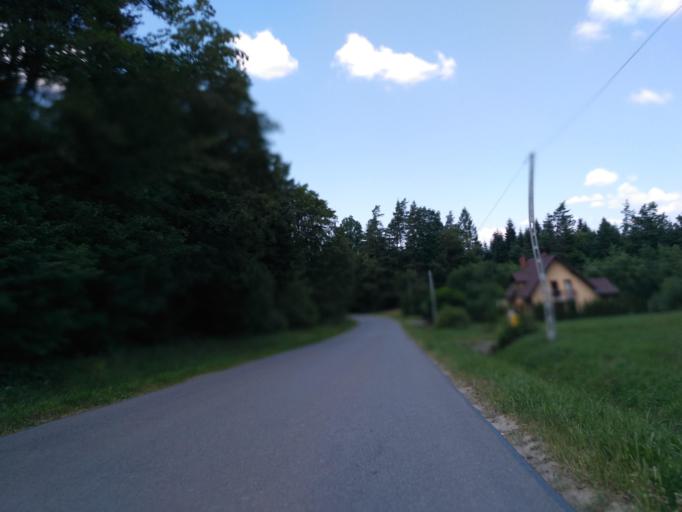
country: PL
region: Subcarpathian Voivodeship
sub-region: Powiat sanocki
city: Niebieszczany
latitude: 49.4881
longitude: 22.1872
